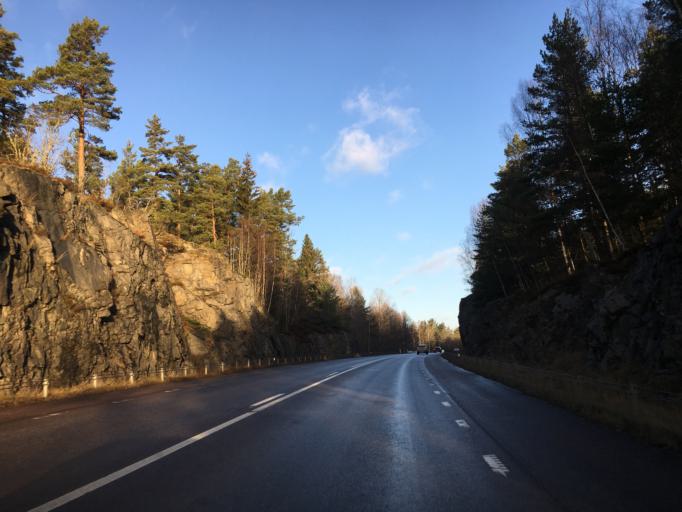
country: SE
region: Kalmar
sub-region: Vasterviks Kommun
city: Ankarsrum
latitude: 57.6677
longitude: 16.4416
